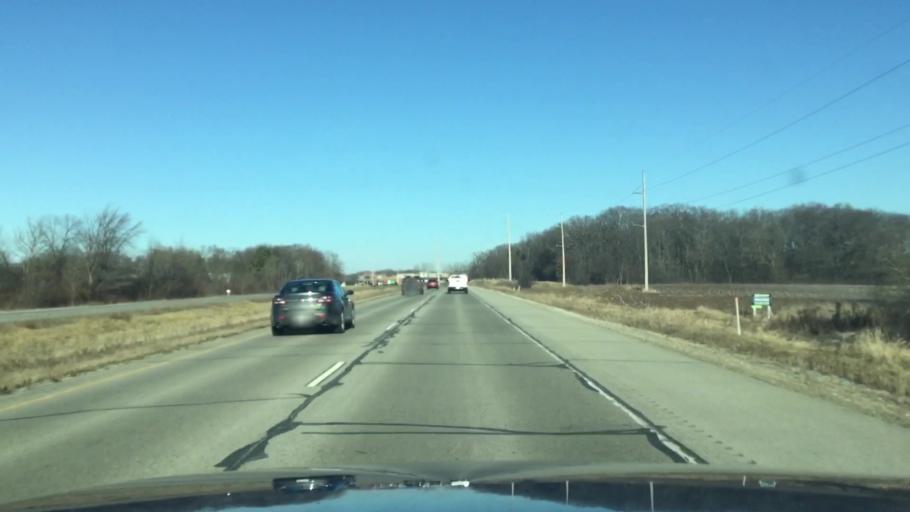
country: US
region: Wisconsin
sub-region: Racine County
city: Waterford
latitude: 42.7586
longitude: -88.2024
